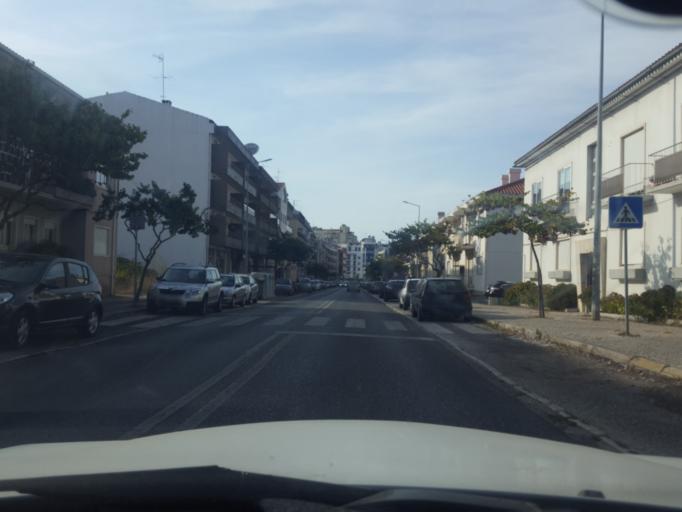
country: PT
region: Leiria
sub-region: Leiria
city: Leiria
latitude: 39.7373
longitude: -8.8000
